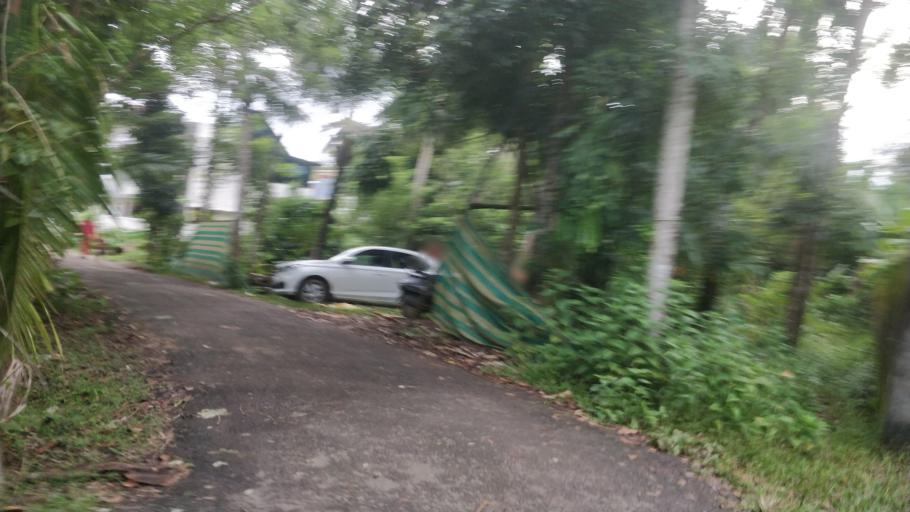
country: IN
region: Kerala
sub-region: Alappuzha
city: Shertallai
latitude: 9.6991
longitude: 76.3599
